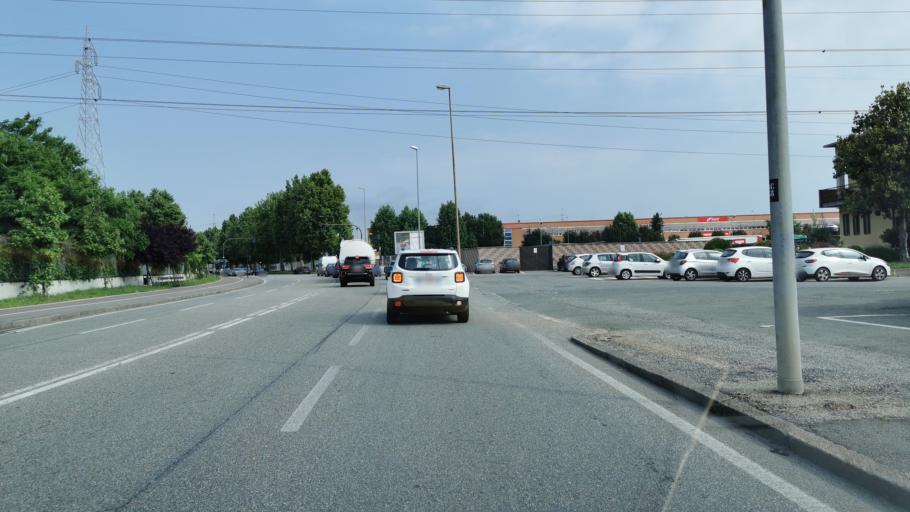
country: IT
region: Piedmont
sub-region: Provincia di Torino
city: Turin
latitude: 45.1045
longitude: 7.7195
